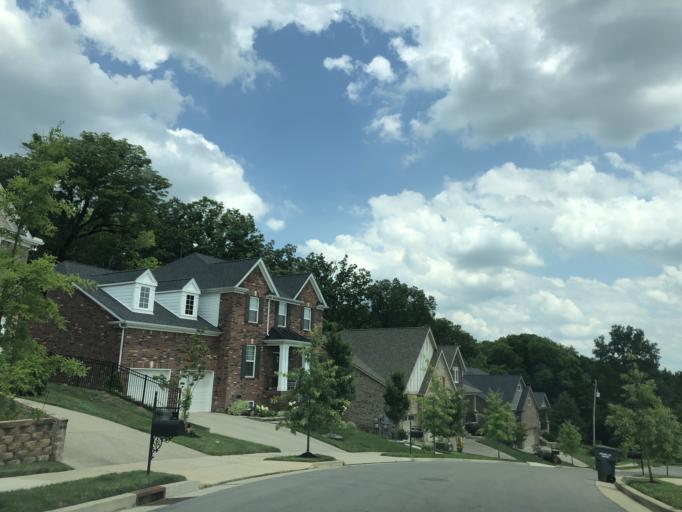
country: US
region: Tennessee
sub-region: Williamson County
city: Brentwood Estates
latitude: 36.0268
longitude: -86.7264
